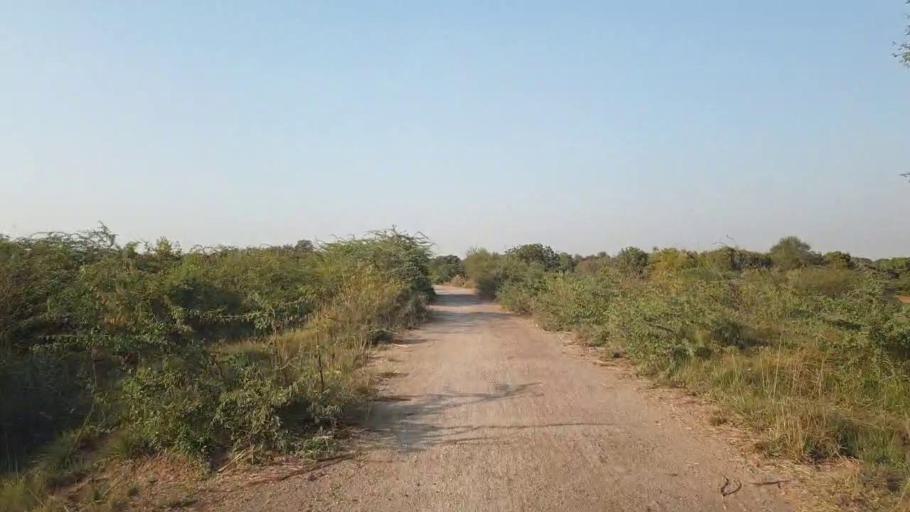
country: PK
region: Sindh
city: Mirpur Khas
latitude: 25.4364
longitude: 68.9100
